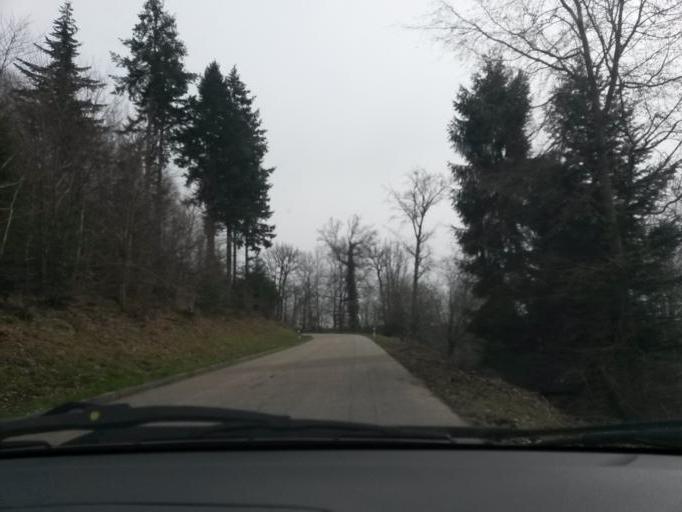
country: DE
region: Baden-Wuerttemberg
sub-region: Freiburg Region
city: Hohberg
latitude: 48.3107
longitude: 7.8868
